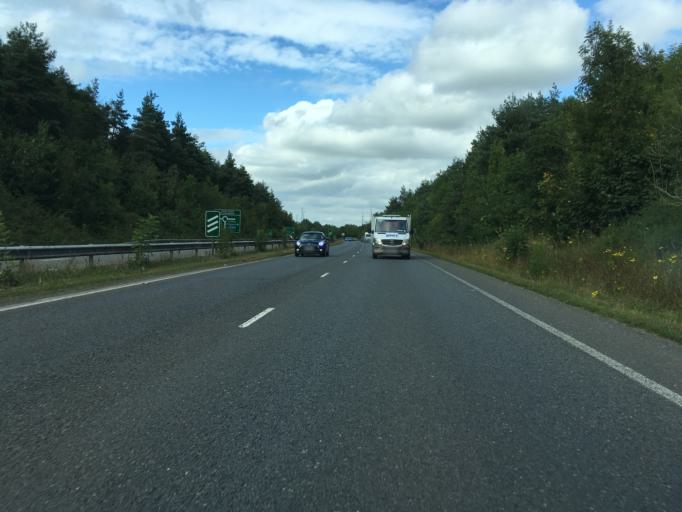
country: GB
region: England
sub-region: West Sussex
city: Horsham
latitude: 51.0846
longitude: -0.3338
